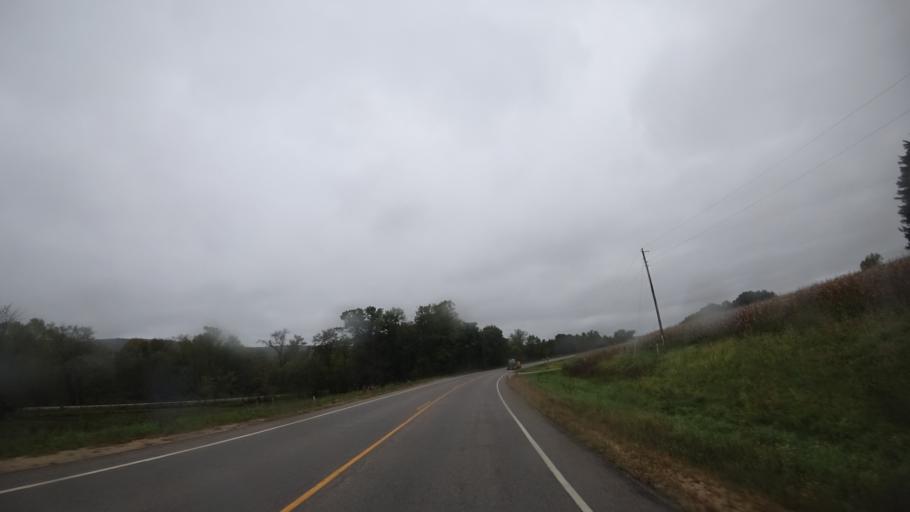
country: US
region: Wisconsin
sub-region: Crawford County
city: Prairie du Chien
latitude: 43.0348
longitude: -90.9889
